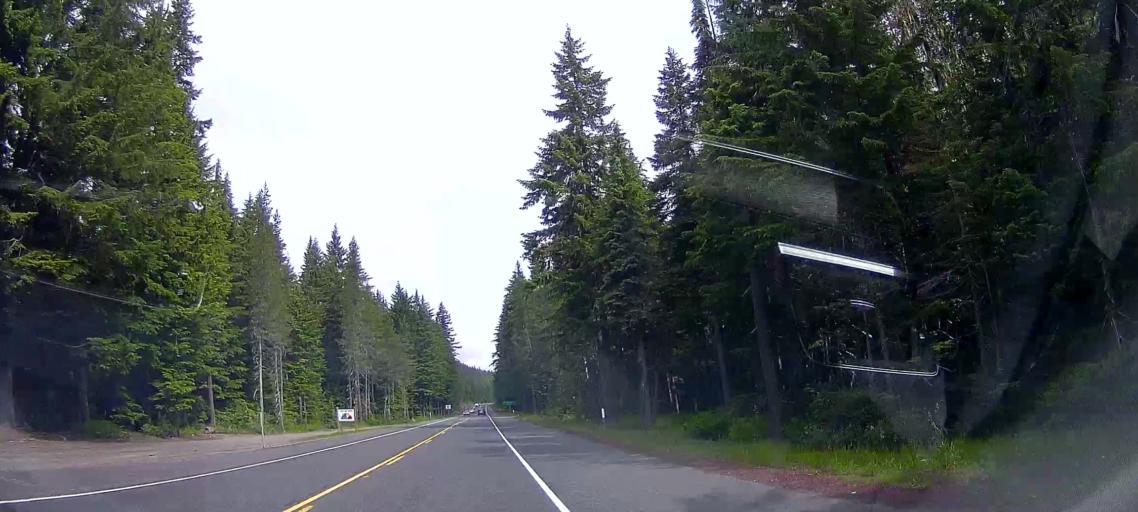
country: US
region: Oregon
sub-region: Clackamas County
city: Mount Hood Village
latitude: 45.2621
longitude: -121.7144
